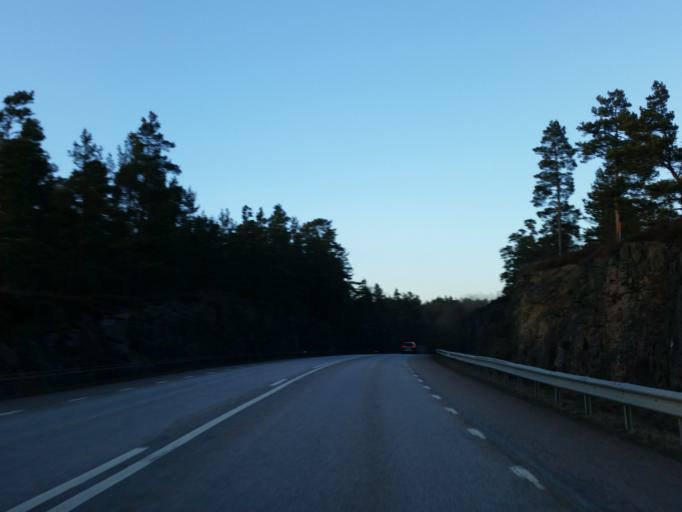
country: SE
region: Kalmar
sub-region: Oskarshamns Kommun
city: Oskarshamn
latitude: 57.4384
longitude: 16.4912
